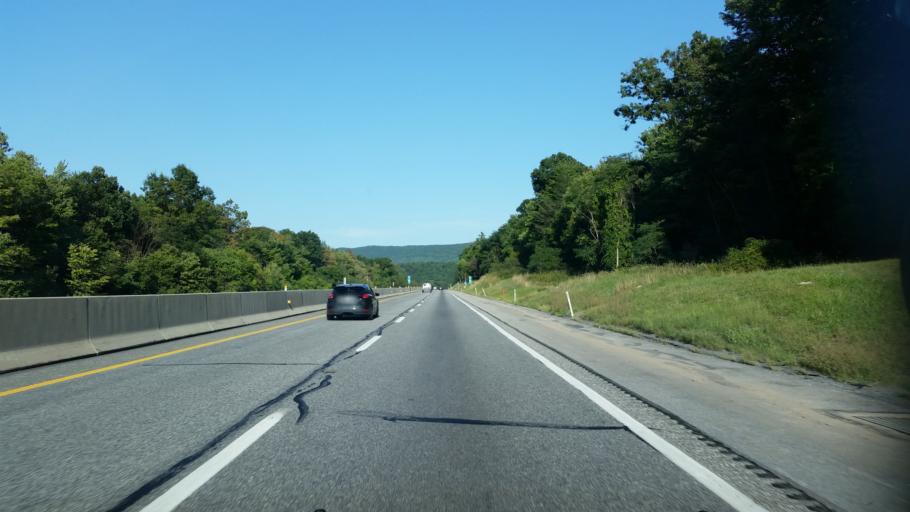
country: US
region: Pennsylvania
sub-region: Fulton County
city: McConnellsburg
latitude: 40.0742
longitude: -77.9080
